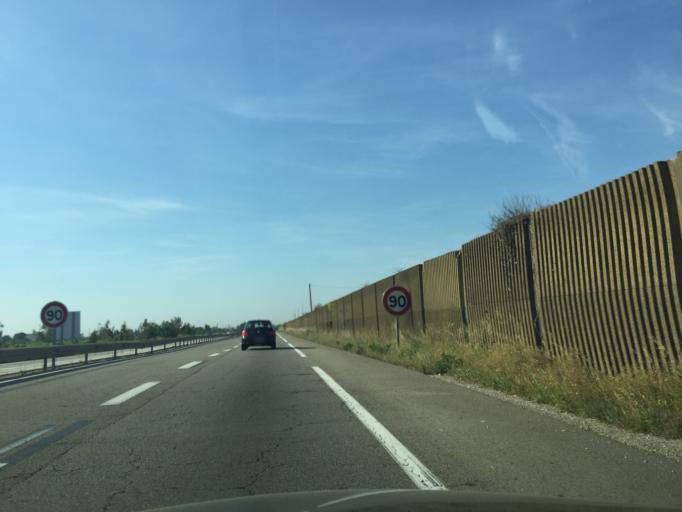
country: FR
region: Provence-Alpes-Cote d'Azur
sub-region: Departement des Bouches-du-Rhone
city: Fos-sur-Mer
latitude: 43.4348
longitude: 4.9416
